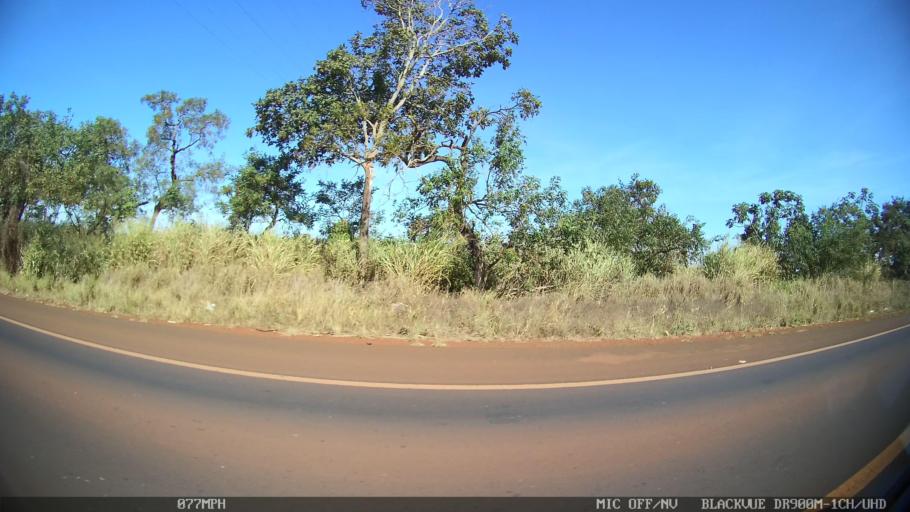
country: BR
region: Sao Paulo
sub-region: Guaira
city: Guaira
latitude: -20.4444
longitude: -48.3667
